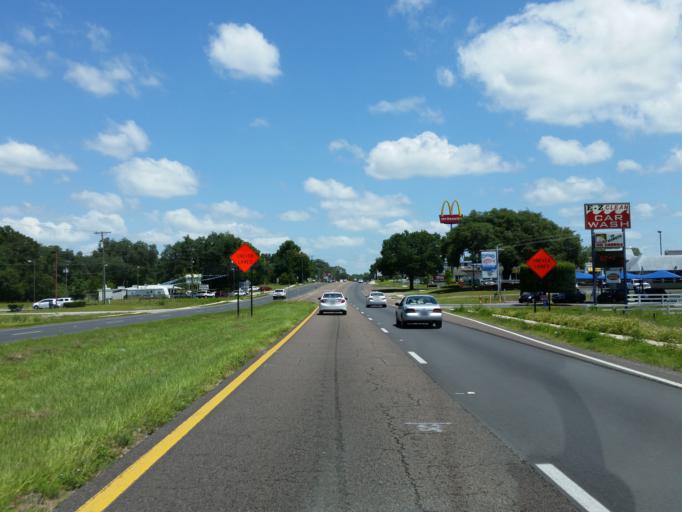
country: US
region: Florida
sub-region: Pasco County
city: Dade City
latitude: 28.3464
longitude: -82.1874
